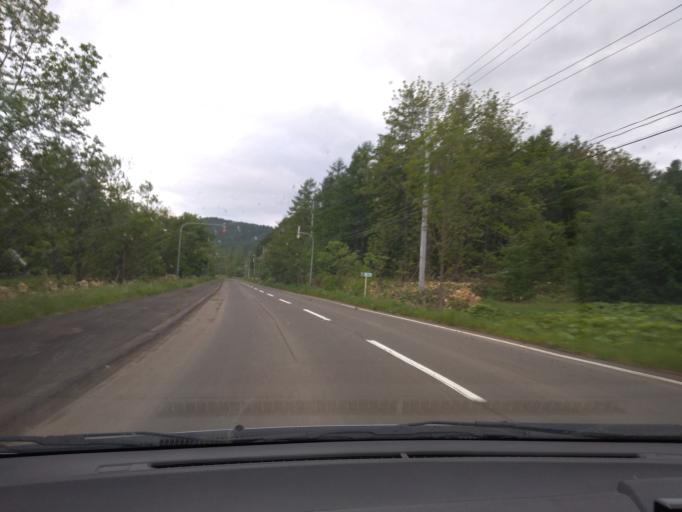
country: JP
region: Hokkaido
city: Shimo-furano
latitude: 43.1759
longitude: 142.5210
